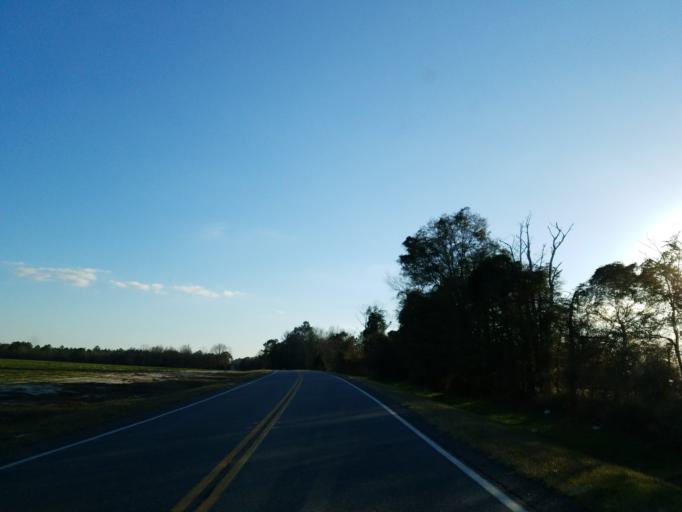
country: US
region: Georgia
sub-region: Crisp County
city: Cordele
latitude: 31.8104
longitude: -83.8015
